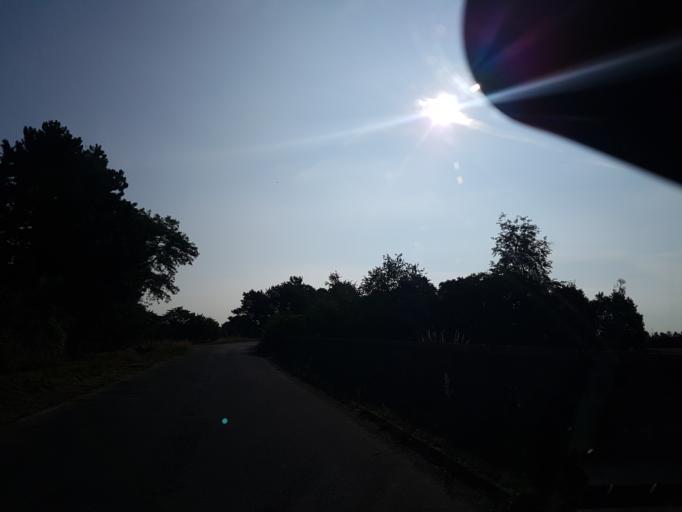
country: DE
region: Saxony-Anhalt
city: Kropstadt
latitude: 52.0325
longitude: 12.7618
